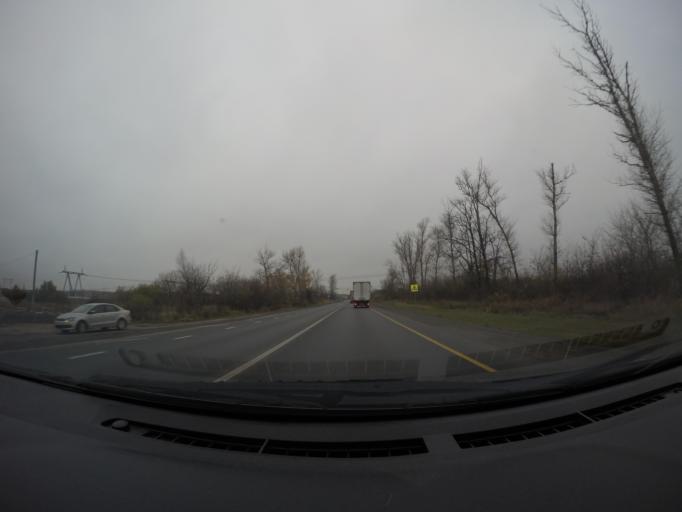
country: RU
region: Moskovskaya
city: Bronnitsy
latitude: 55.3886
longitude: 38.1972
